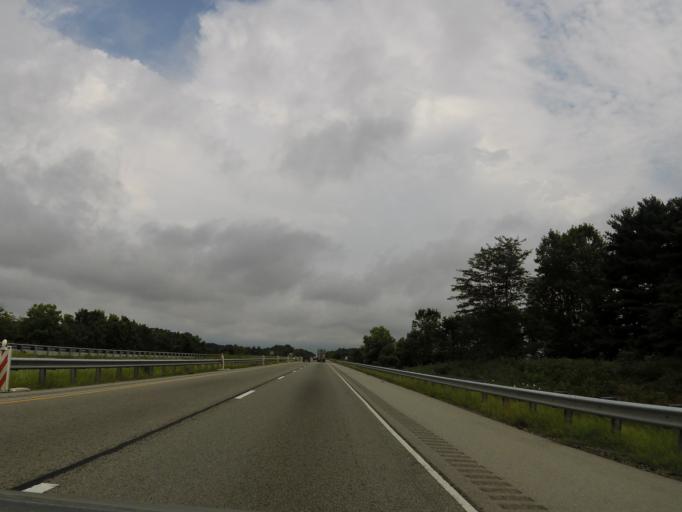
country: US
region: Illinois
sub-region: Jefferson County
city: Ina
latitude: 38.0983
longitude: -88.9114
